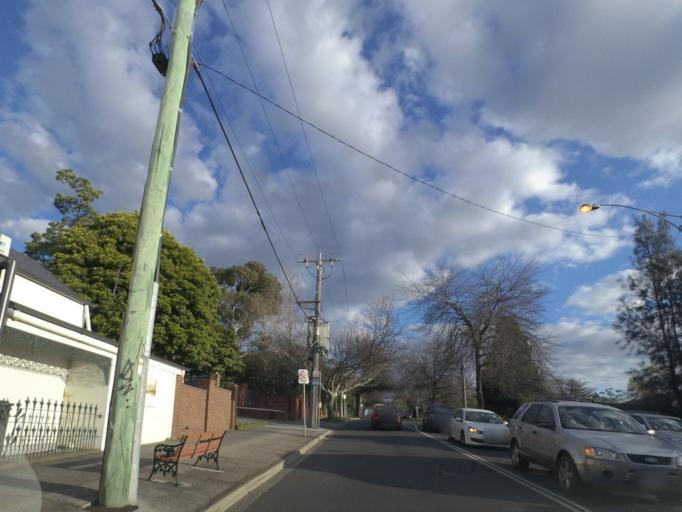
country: AU
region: Victoria
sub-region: Whitehorse
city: Surrey Hills
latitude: -37.8261
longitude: 145.0973
